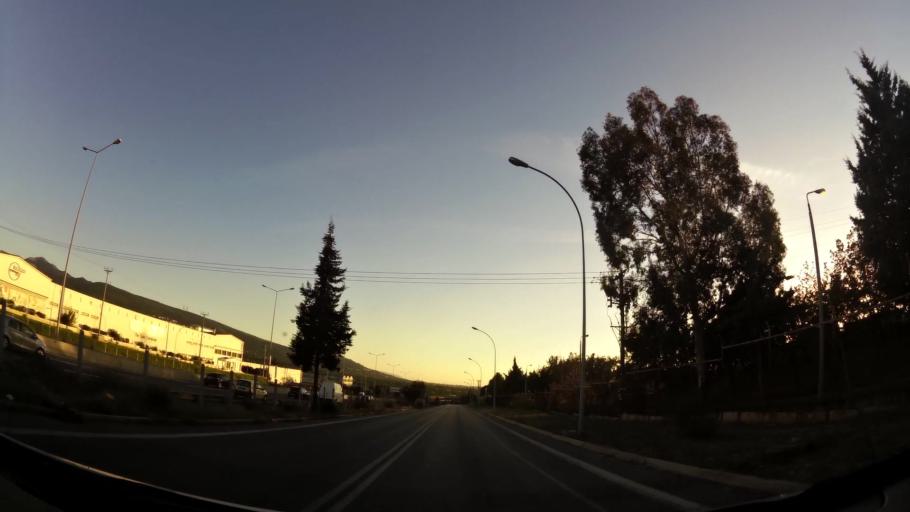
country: GR
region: Attica
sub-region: Nomarchia Anatolikis Attikis
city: Kryoneri
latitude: 38.1301
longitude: 23.8383
